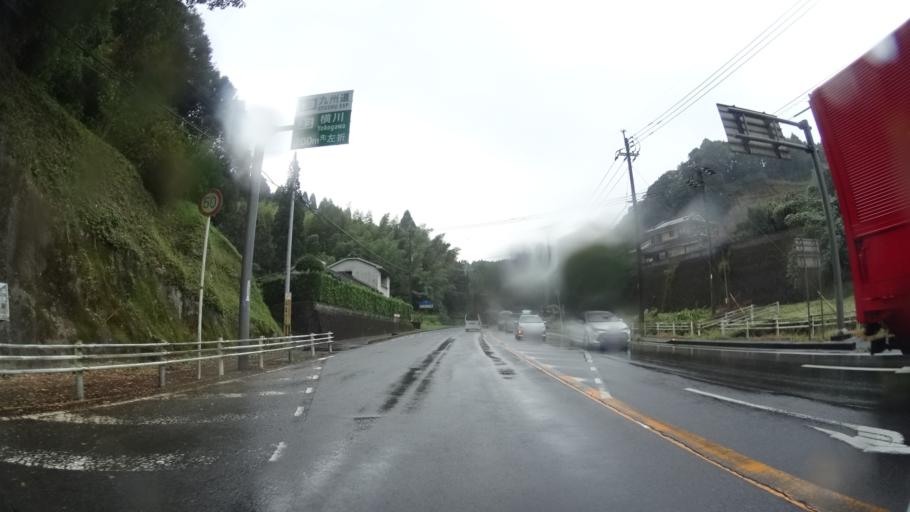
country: JP
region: Kagoshima
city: Kajiki
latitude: 31.9011
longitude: 130.7000
